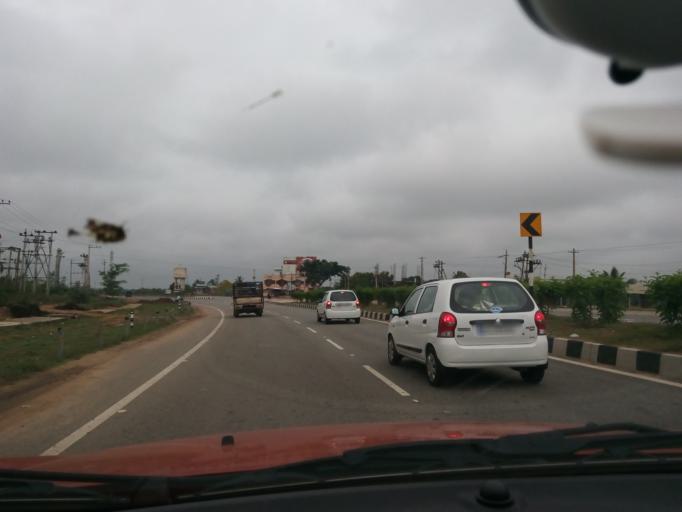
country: IN
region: Karnataka
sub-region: Hassan
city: Shravanabelagola
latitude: 12.9528
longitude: 76.5690
